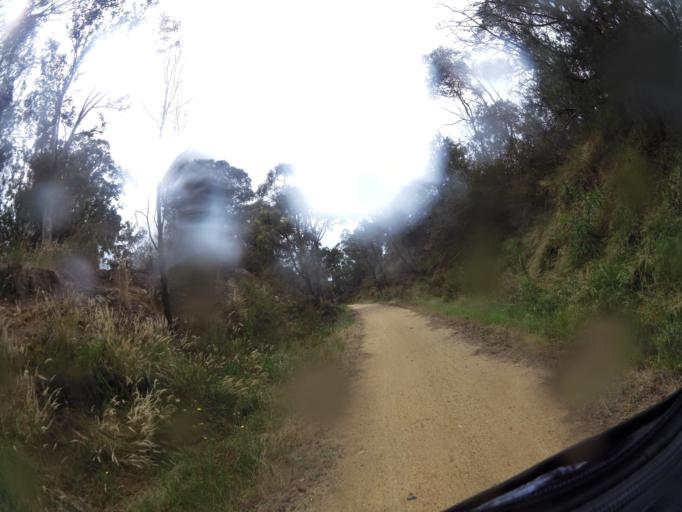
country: AU
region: Victoria
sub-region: East Gippsland
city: Lakes Entrance
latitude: -37.7601
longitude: 147.8169
